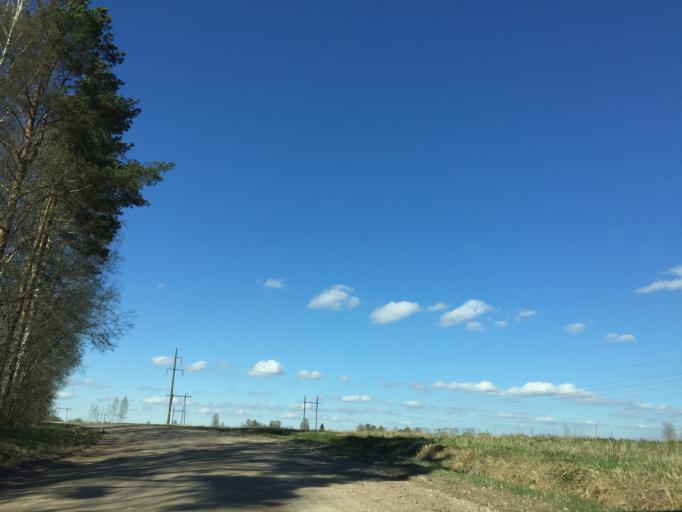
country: EE
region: Valgamaa
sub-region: Valga linn
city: Valga
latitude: 57.8518
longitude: 26.1705
